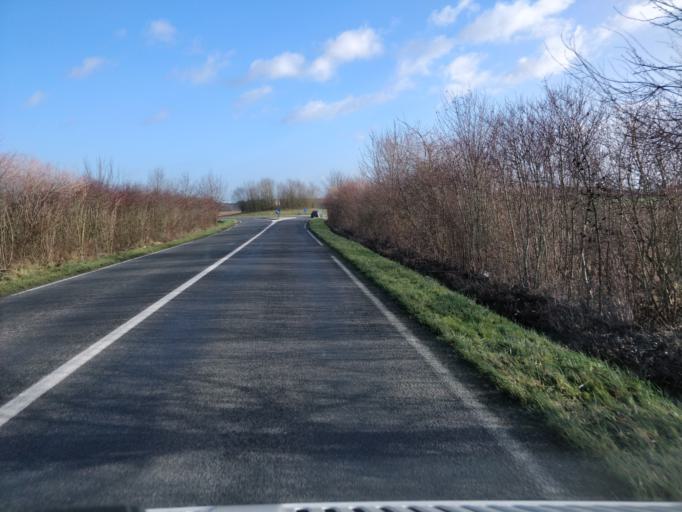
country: FR
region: Ile-de-France
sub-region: Departement de Seine-et-Marne
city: Lorrez-le-Bocage-Preaux
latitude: 48.2194
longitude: 2.8916
